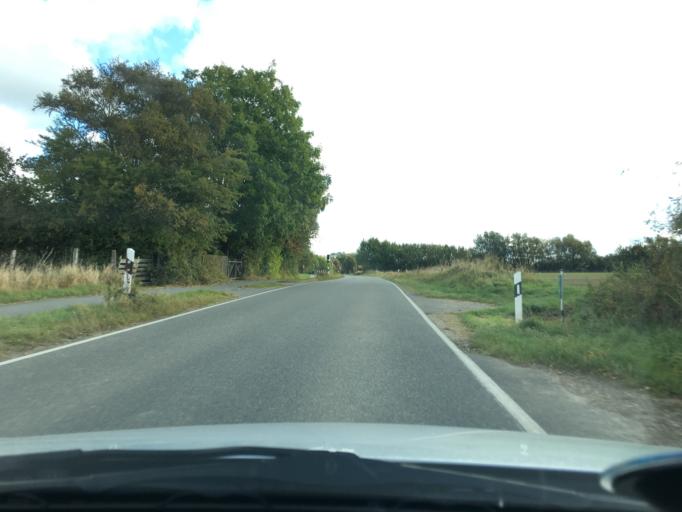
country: DE
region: Schleswig-Holstein
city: Stein
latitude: 54.4152
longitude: 10.2610
